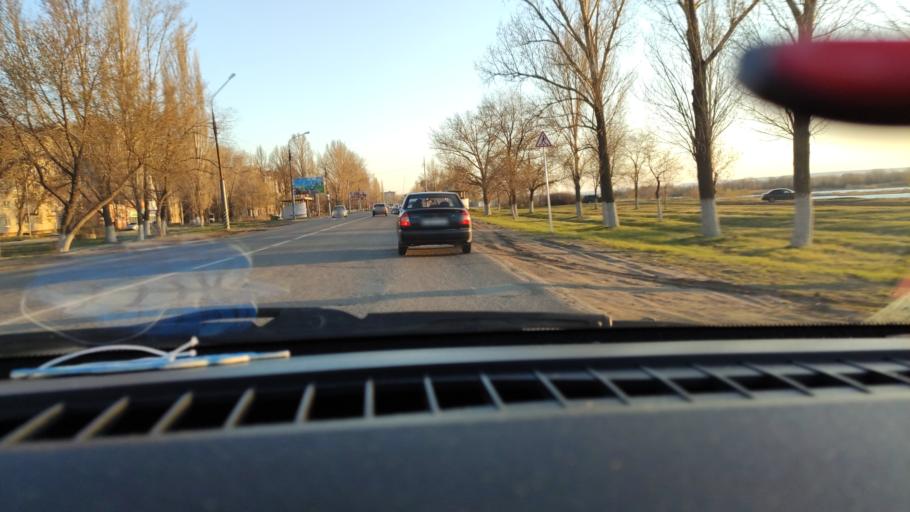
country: RU
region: Saratov
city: Engel's
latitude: 51.4544
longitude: 46.0855
